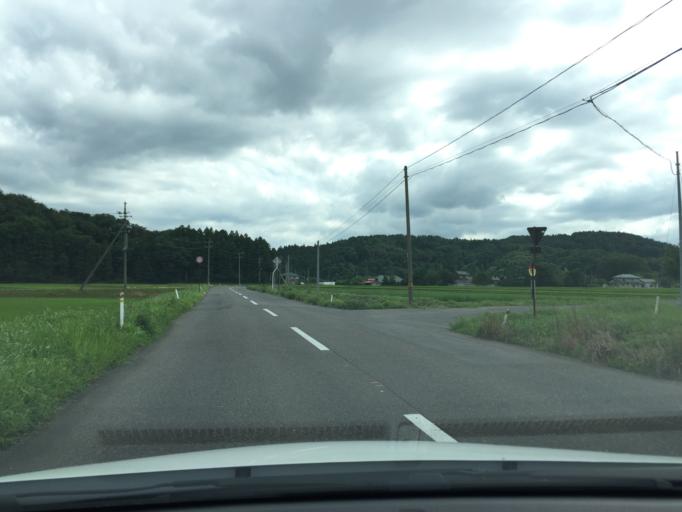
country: JP
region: Fukushima
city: Sukagawa
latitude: 37.3114
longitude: 140.2084
